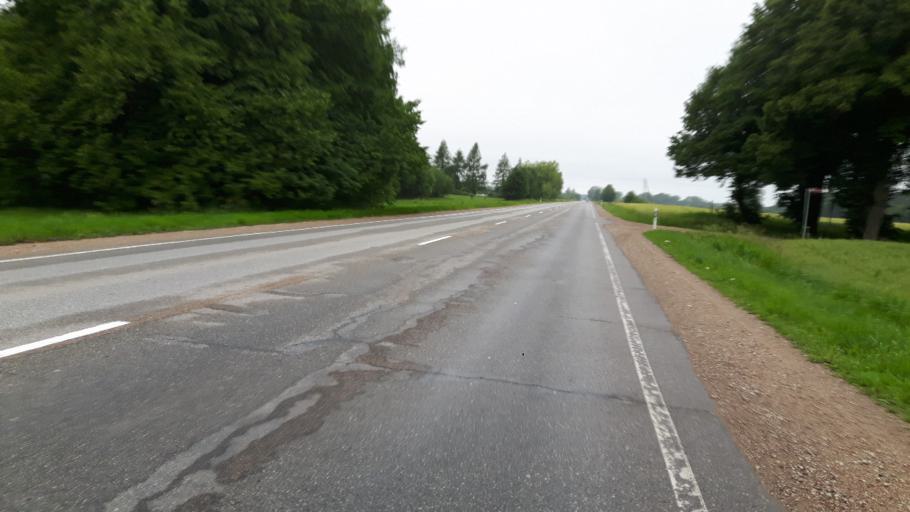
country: LV
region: Nica
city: Nica
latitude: 56.3481
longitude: 21.0534
